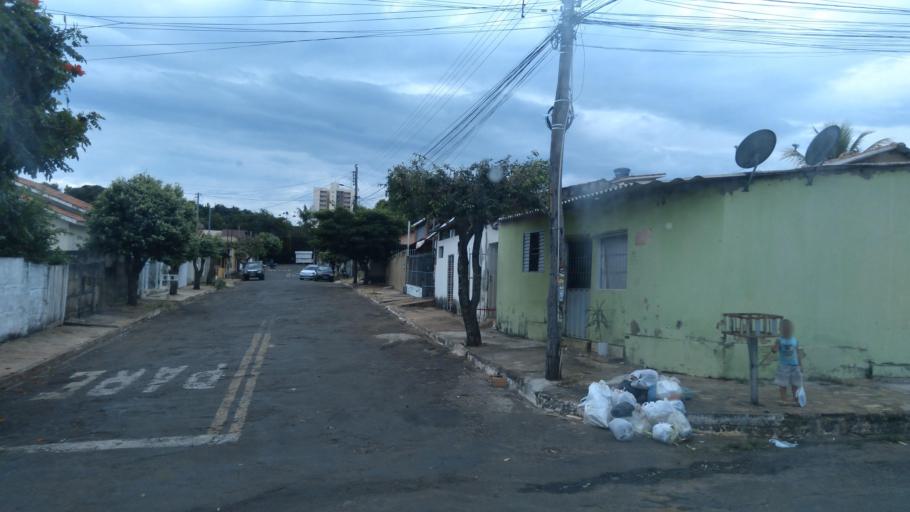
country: BR
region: Goias
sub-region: Mineiros
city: Mineiros
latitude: -17.5693
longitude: -52.5623
